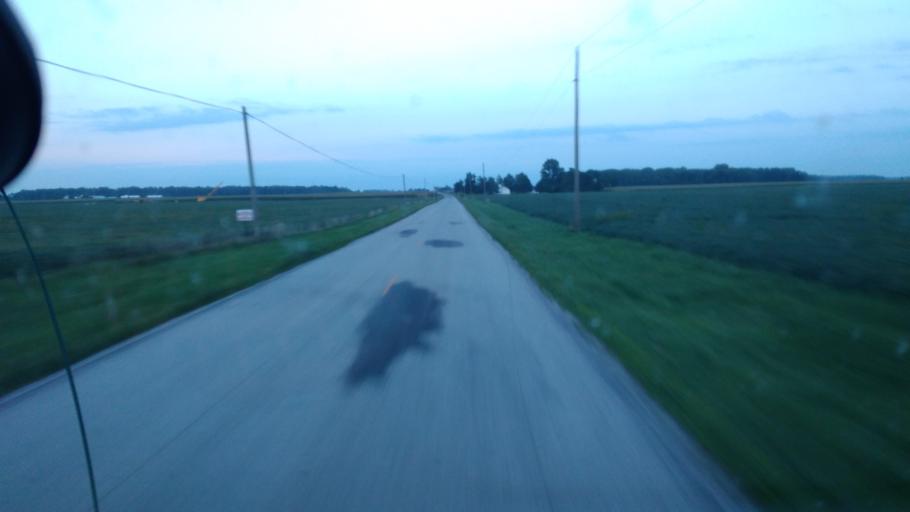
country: US
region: Ohio
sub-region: Hardin County
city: Kenton
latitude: 40.6723
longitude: -83.5102
